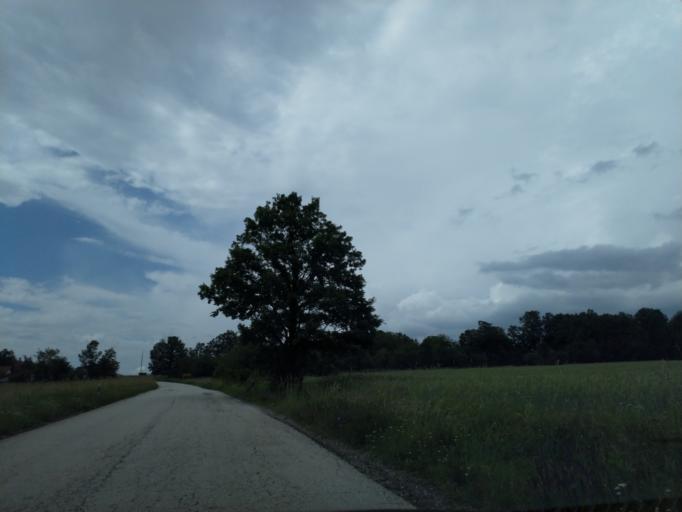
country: RS
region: Central Serbia
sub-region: Zajecarski Okrug
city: Boljevac
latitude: 43.8842
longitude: 21.9709
